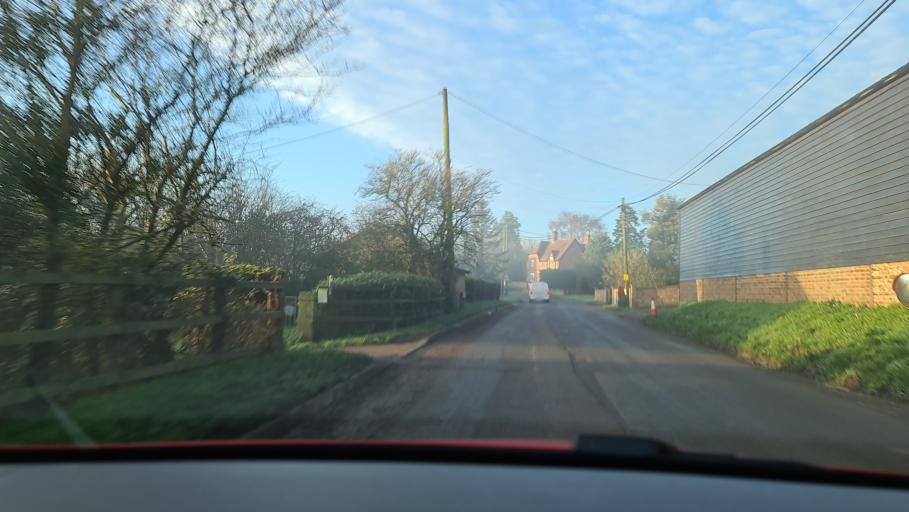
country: GB
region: England
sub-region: Buckinghamshire
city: Long Crendon
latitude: 51.8241
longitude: -0.9746
